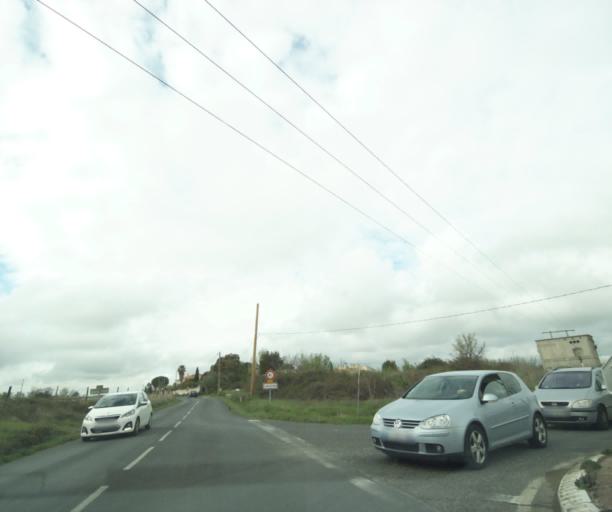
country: FR
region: Languedoc-Roussillon
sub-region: Departement de l'Herault
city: Saussan
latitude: 43.5639
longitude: 3.7755
